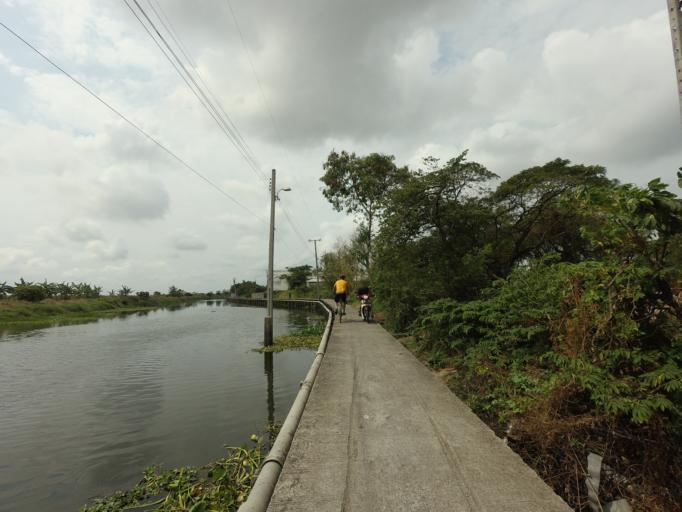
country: TH
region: Bangkok
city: Lat Krabang
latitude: 13.6798
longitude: 100.7289
